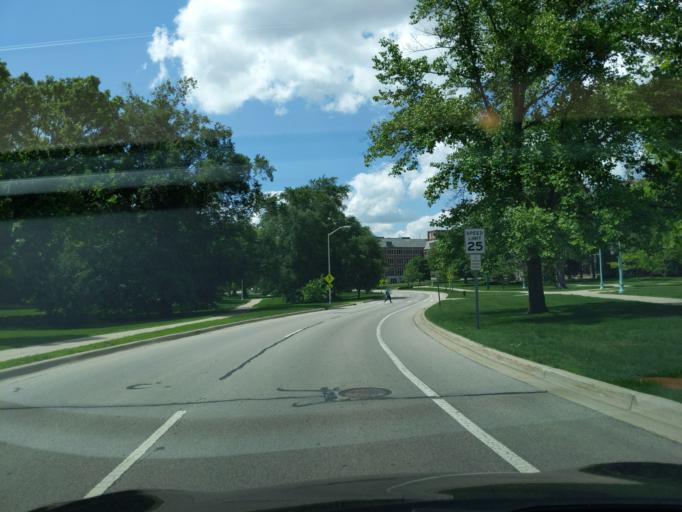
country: US
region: Michigan
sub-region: Ingham County
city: East Lansing
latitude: 42.7326
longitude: -84.4806
